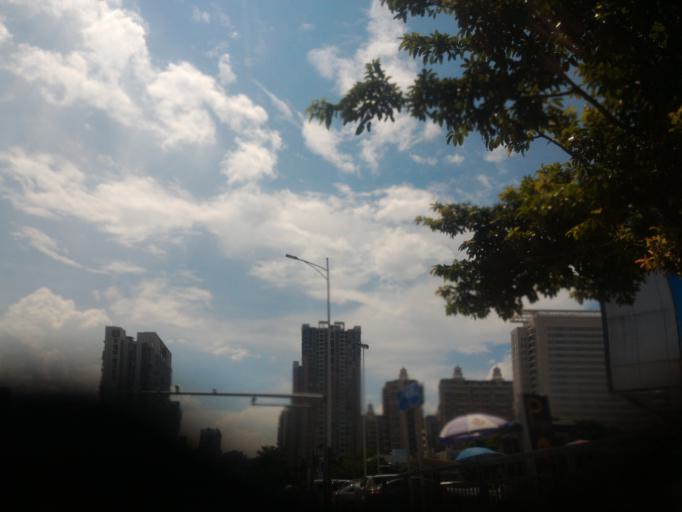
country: CN
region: Guangdong
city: Xixiang
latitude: 22.5681
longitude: 113.8701
